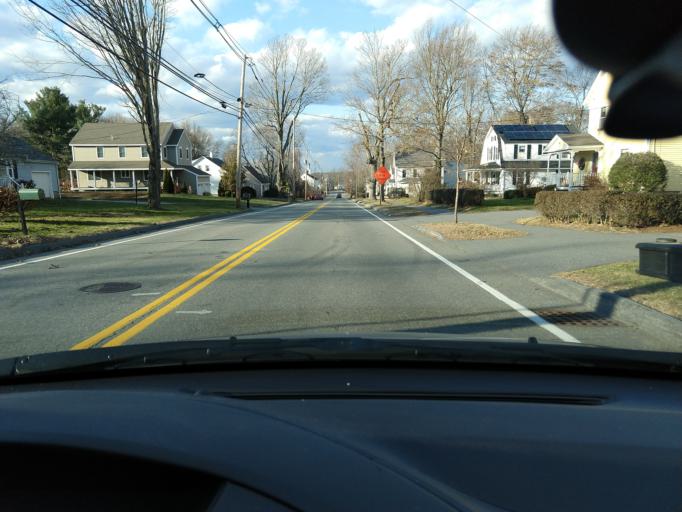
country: US
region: Massachusetts
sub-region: Middlesex County
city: Littleton Common
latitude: 42.5432
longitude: -71.4715
